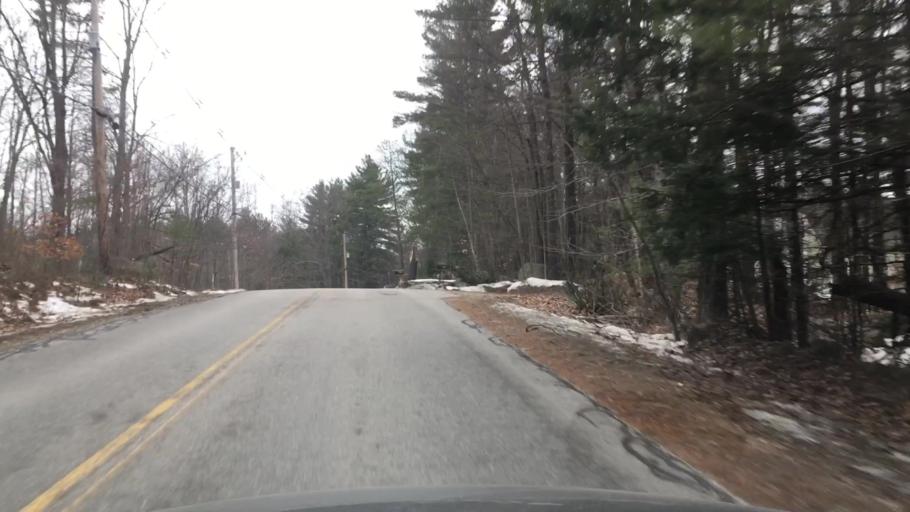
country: US
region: New Hampshire
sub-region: Hillsborough County
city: New Boston
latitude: 42.9759
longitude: -71.6366
